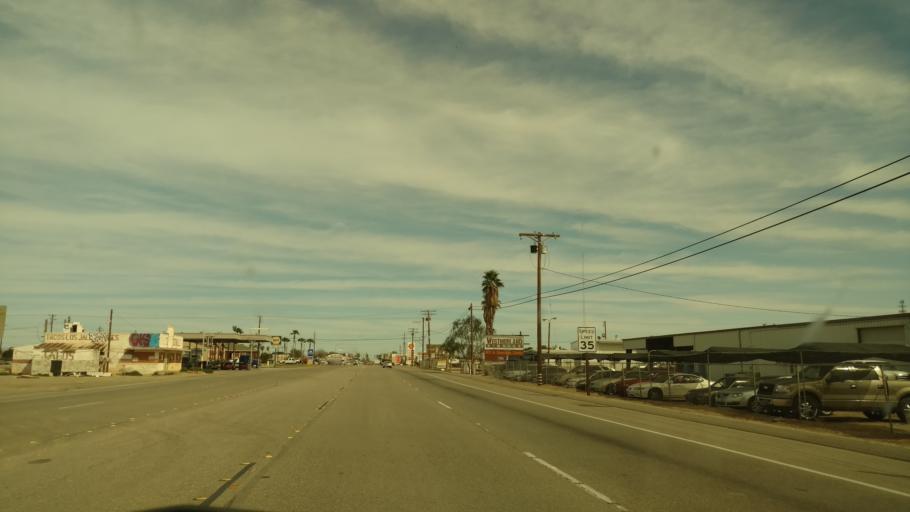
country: US
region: California
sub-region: Imperial County
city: Westmorland
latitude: 33.0373
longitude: -115.6281
